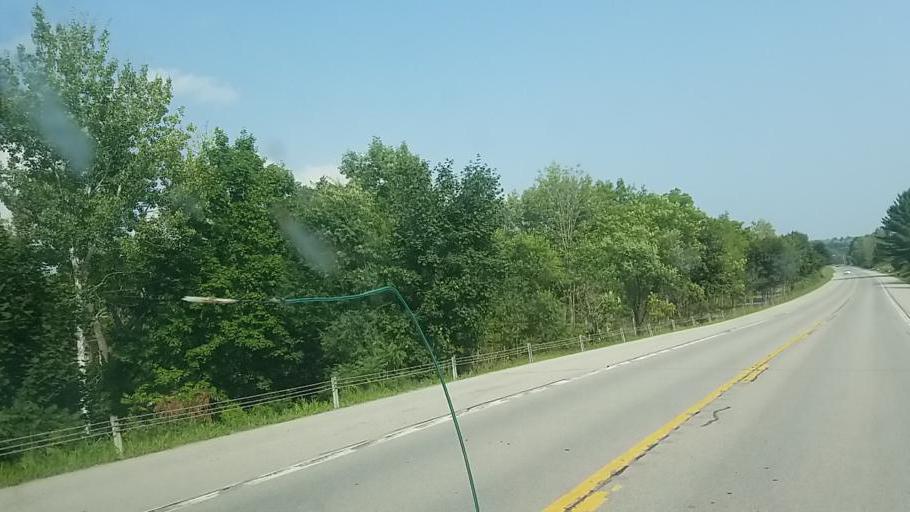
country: US
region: New York
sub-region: Montgomery County
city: Tribes Hill
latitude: 42.9338
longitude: -74.3274
